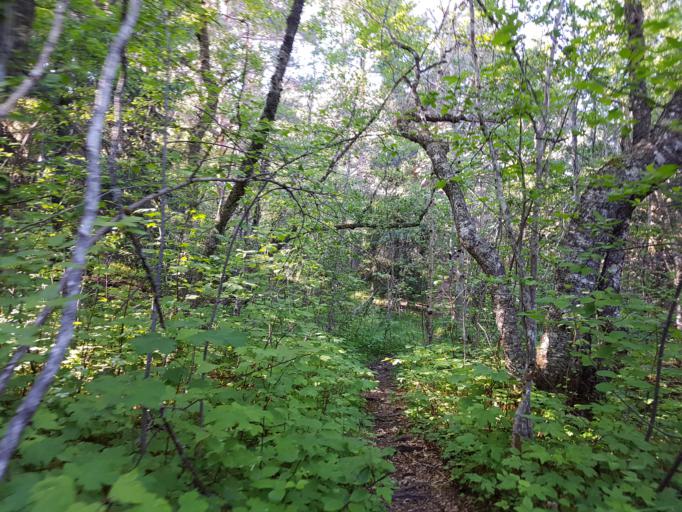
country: NO
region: Sor-Trondelag
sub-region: Trondheim
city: Trondheim
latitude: 63.4206
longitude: 10.3638
